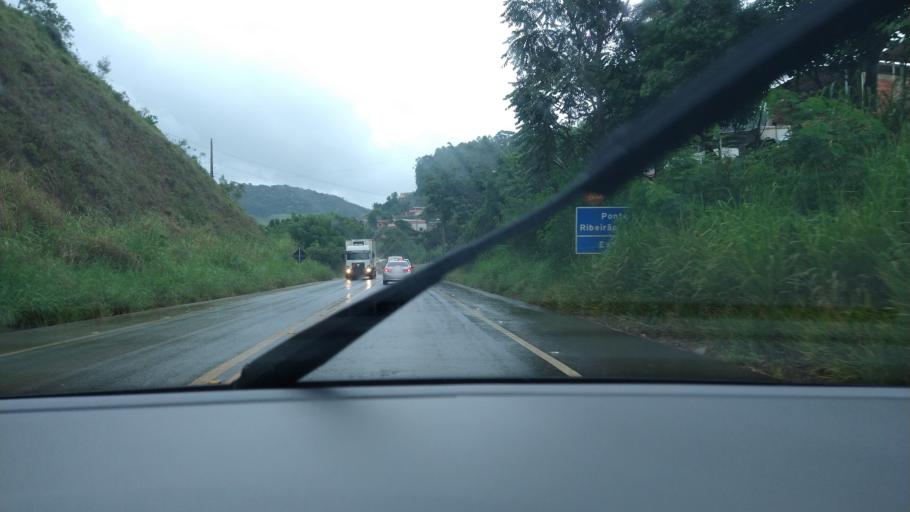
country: BR
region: Minas Gerais
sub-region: Vicosa
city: Vicosa
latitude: -20.6399
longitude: -42.8662
